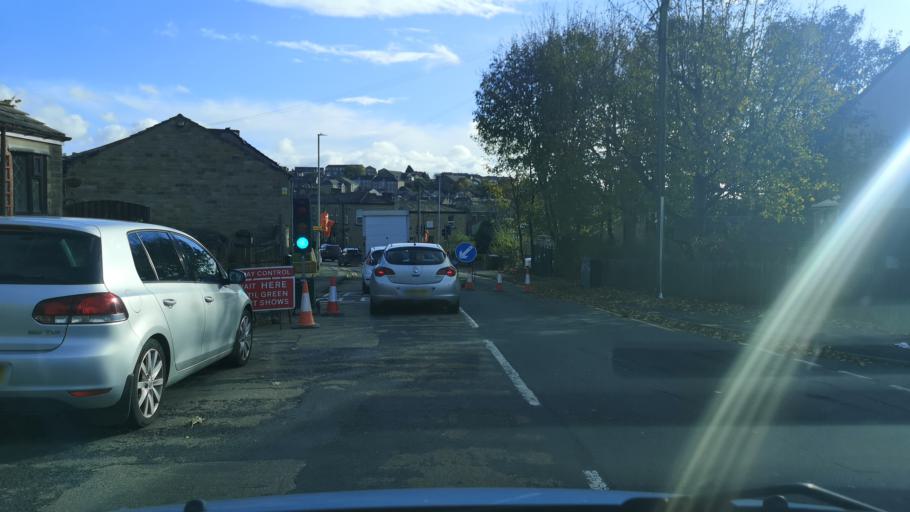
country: GB
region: England
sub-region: Kirklees
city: Heckmondwike
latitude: 53.7113
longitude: -1.6599
